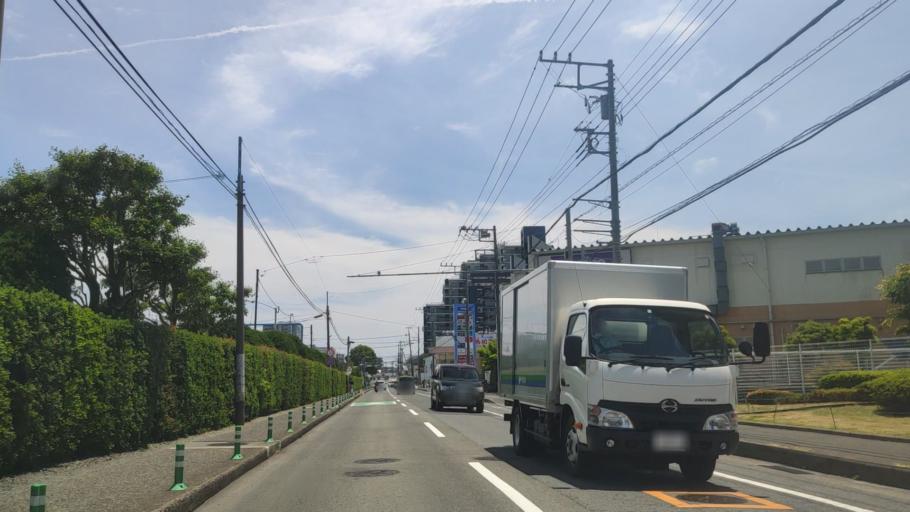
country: JP
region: Kanagawa
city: Chigasaki
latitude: 35.3359
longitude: 139.3988
